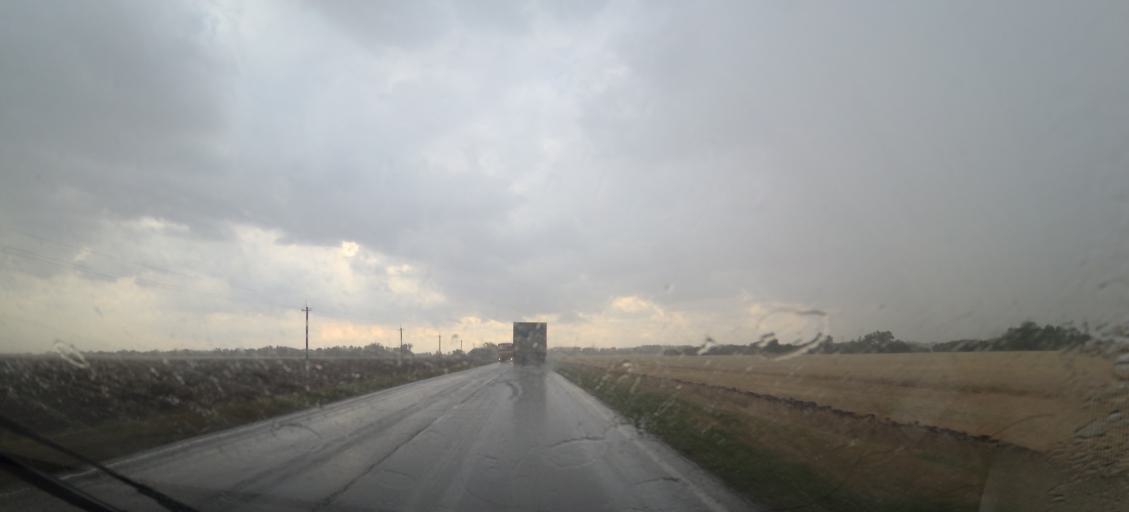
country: RU
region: Rostov
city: Gundorovskiy
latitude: 46.8583
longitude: 41.9405
